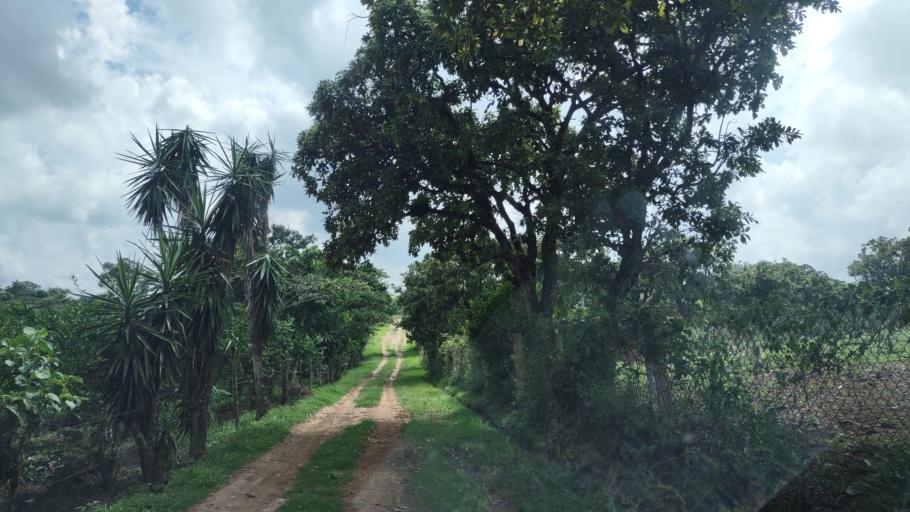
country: MX
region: Veracruz
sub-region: Emiliano Zapata
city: Jacarandas
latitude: 19.4735
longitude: -96.8386
